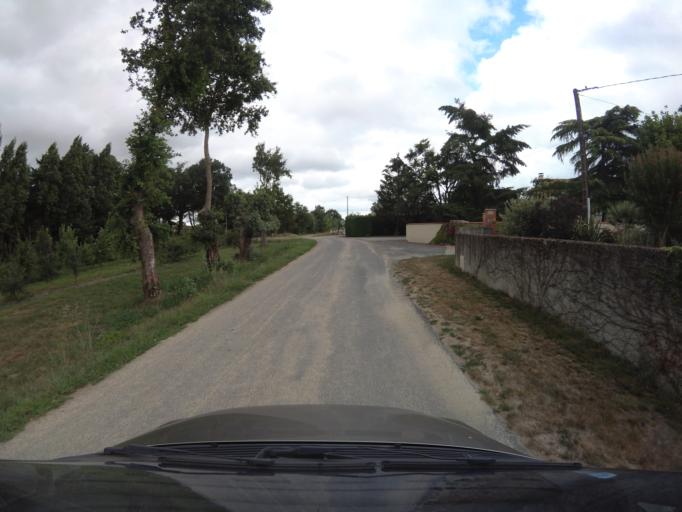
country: FR
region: Pays de la Loire
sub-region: Departement de la Loire-Atlantique
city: La Planche
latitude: 47.0064
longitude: -1.4513
